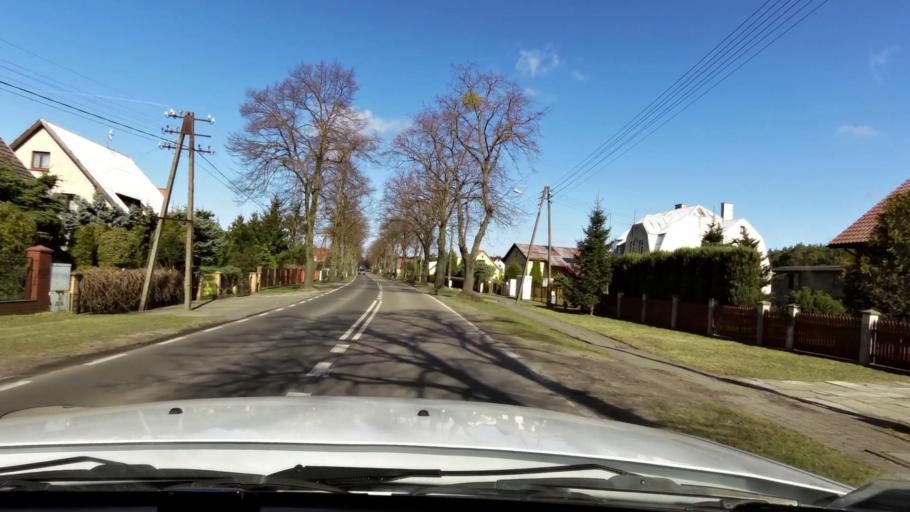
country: PL
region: West Pomeranian Voivodeship
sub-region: Powiat gryfinski
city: Gryfino
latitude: 53.2181
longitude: 14.4933
